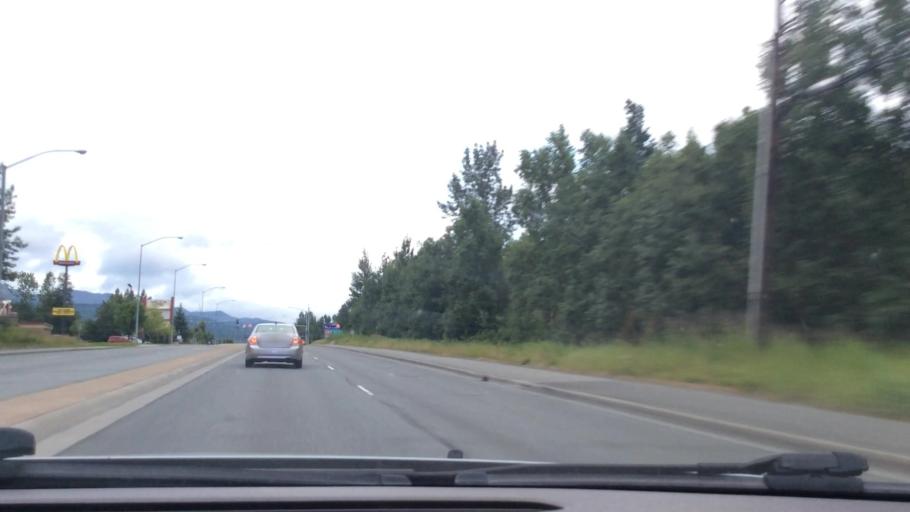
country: US
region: Alaska
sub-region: Anchorage Municipality
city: Elmendorf Air Force Base
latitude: 61.1943
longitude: -149.7336
